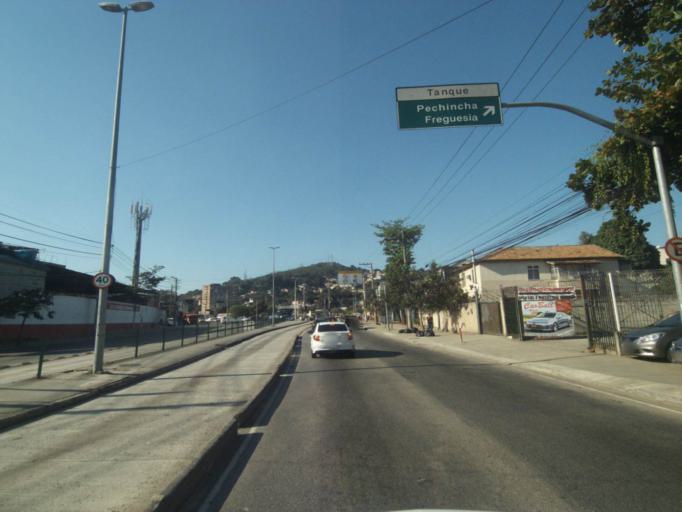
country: BR
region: Rio de Janeiro
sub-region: Sao Joao De Meriti
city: Sao Joao de Meriti
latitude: -22.9172
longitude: -43.3629
